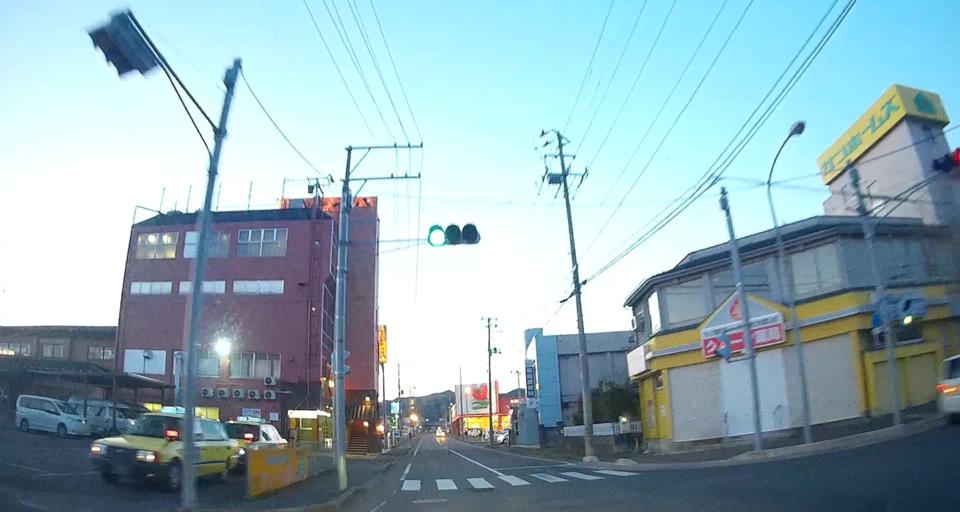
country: JP
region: Aomori
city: Hachinohe
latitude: 40.1905
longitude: 141.7719
